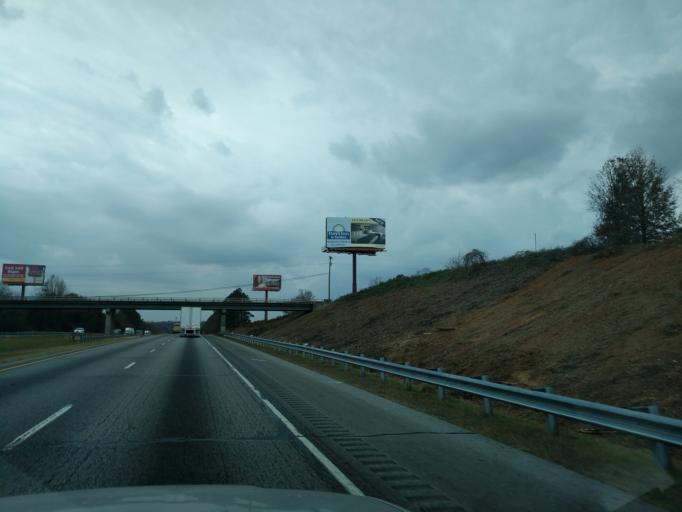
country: US
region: Georgia
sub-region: Franklin County
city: Carnesville
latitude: 34.4075
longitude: -83.1951
